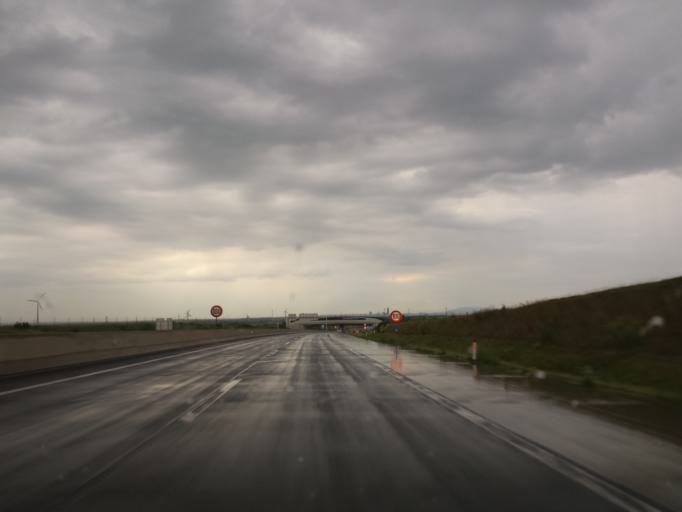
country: AT
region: Lower Austria
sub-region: Politischer Bezirk Mistelbach
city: Grossebersdorf
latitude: 48.3705
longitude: 16.4875
